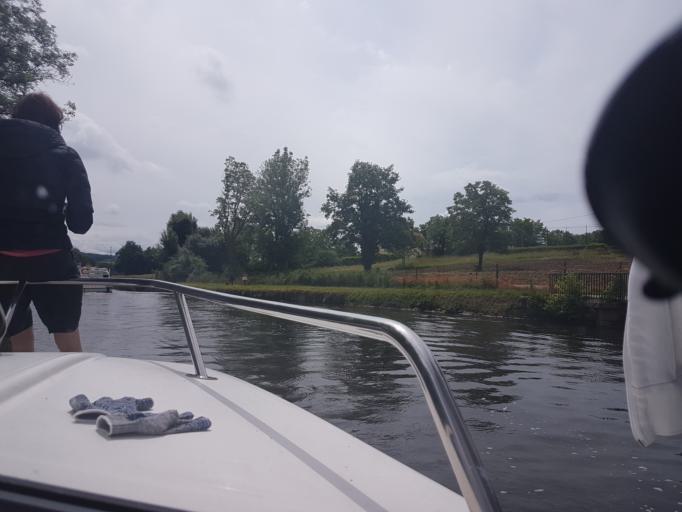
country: FR
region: Bourgogne
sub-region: Departement de l'Yonne
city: Augy
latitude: 47.7838
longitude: 3.5951
